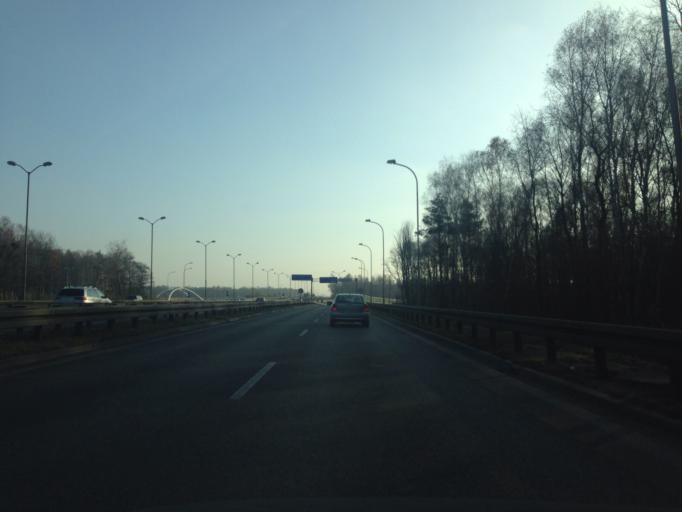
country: PL
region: Silesian Voivodeship
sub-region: Katowice
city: Katowice
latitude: 50.2460
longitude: 19.0502
